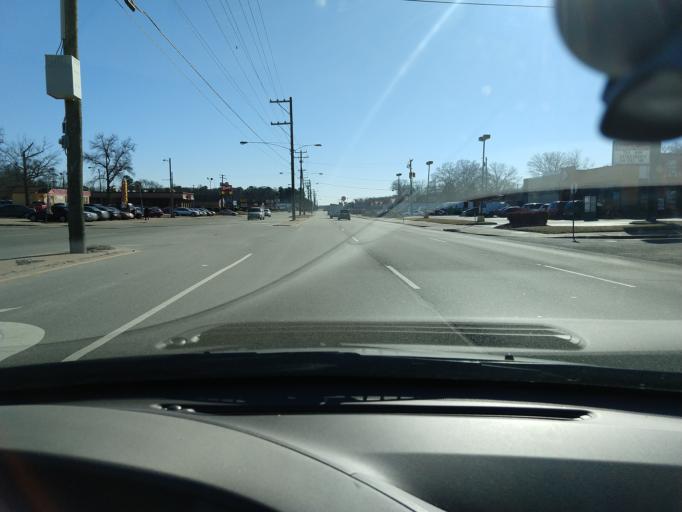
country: US
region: Virginia
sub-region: Chesterfield County
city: Bensley
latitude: 37.4657
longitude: -77.4430
